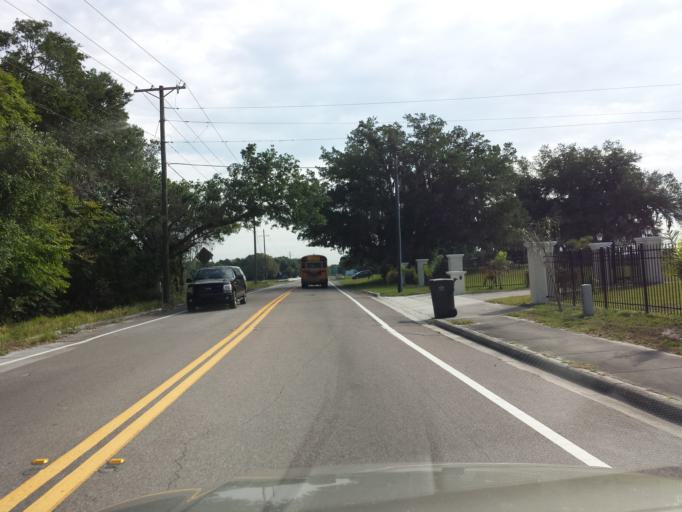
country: US
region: Florida
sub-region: Hillsborough County
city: Temple Terrace
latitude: 28.0352
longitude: -82.3463
